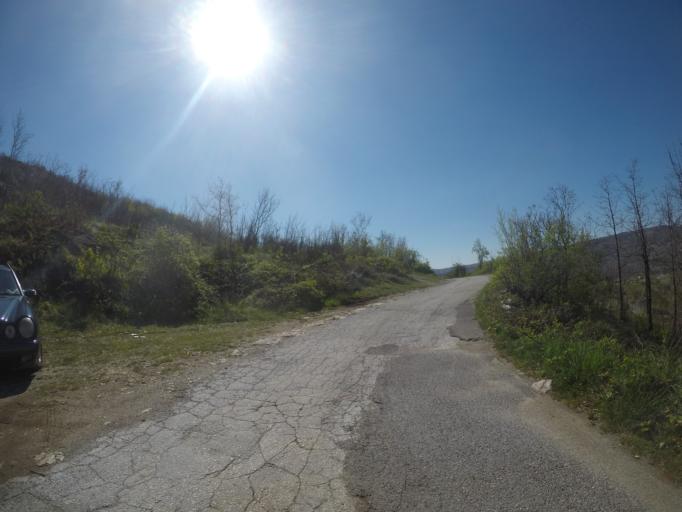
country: ME
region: Danilovgrad
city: Danilovgrad
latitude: 42.5368
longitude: 19.0146
